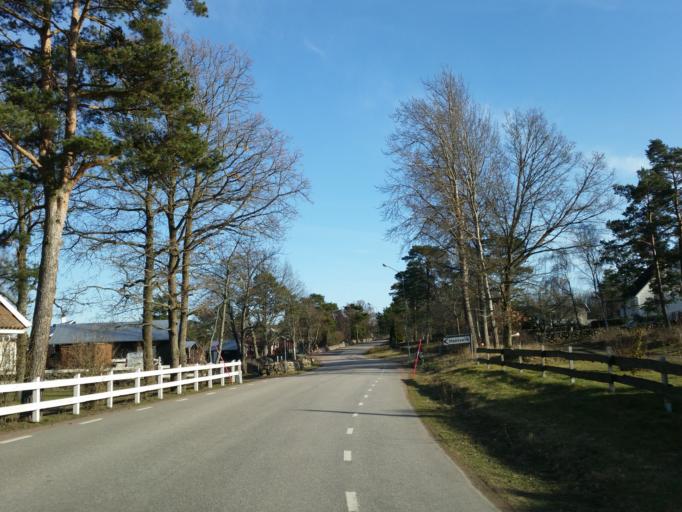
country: SE
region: Kalmar
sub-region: Kalmar Kommun
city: Lindsdal
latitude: 56.7815
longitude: 16.4088
